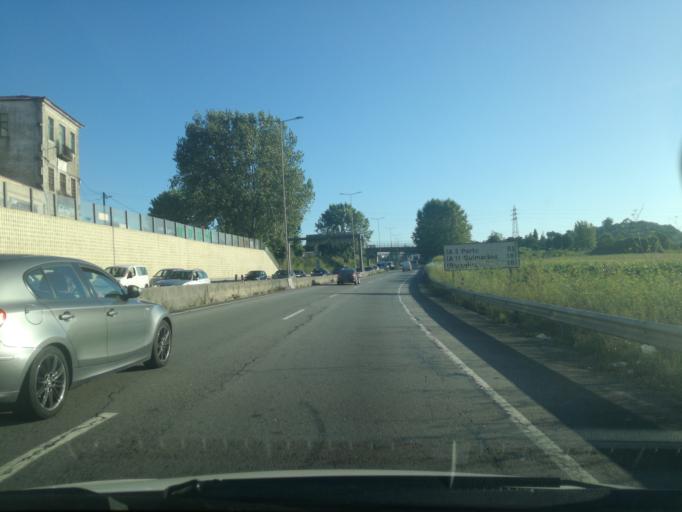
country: PT
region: Braga
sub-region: Braga
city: Braga
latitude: 41.5478
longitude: -8.4358
